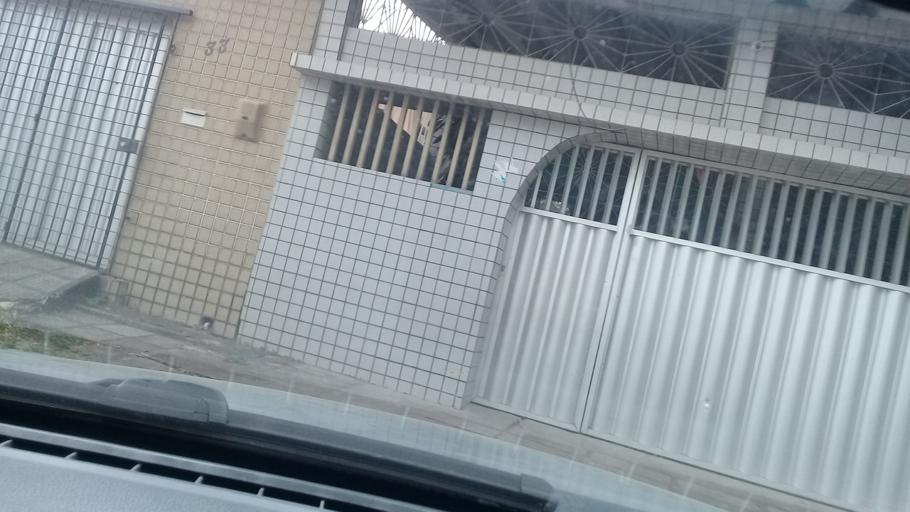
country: BR
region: Pernambuco
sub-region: Jaboatao Dos Guararapes
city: Jaboatao dos Guararapes
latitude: -8.1144
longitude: -34.9508
